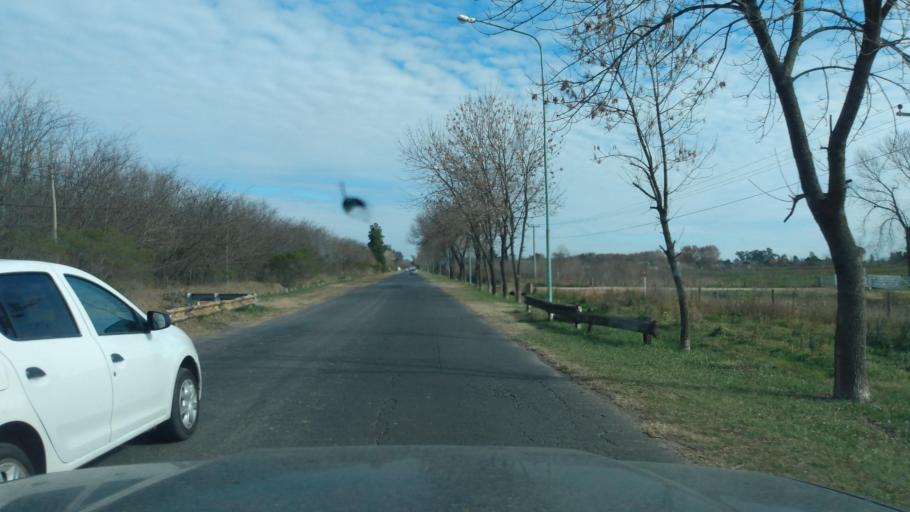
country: AR
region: Buenos Aires
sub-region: Partido de Lujan
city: Lujan
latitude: -34.5764
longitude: -59.1650
